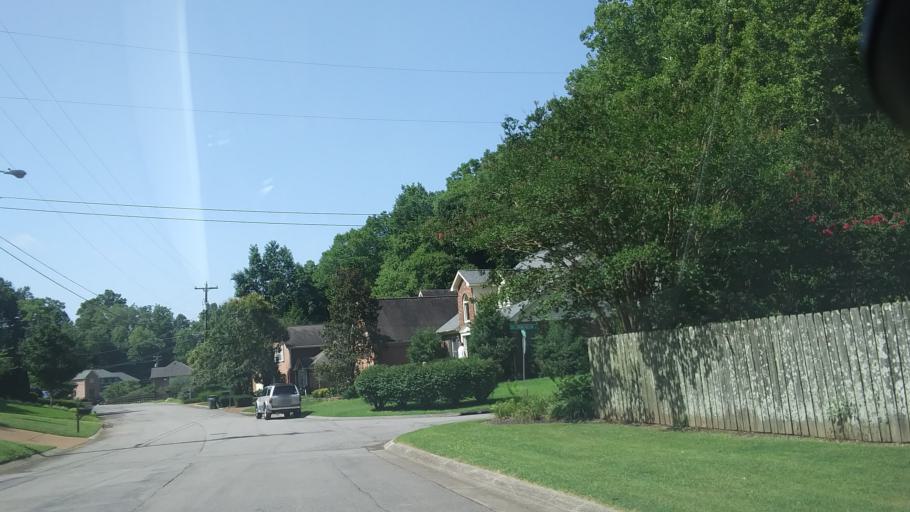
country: US
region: Tennessee
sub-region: Davidson County
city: Belle Meade
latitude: 36.0813
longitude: -86.9244
